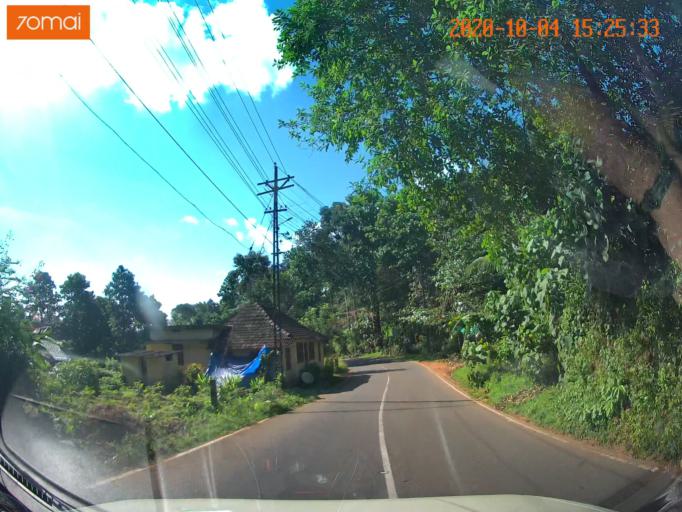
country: IN
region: Kerala
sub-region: Kottayam
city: Palackattumala
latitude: 9.7234
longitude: 76.6481
